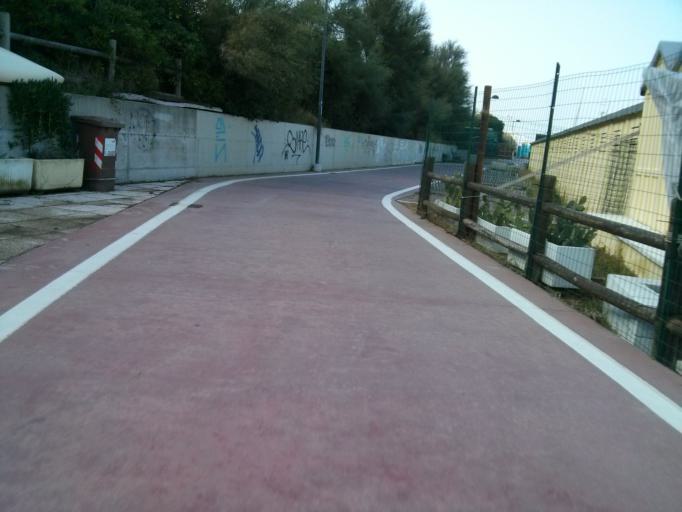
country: IT
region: The Marches
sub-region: Provincia di Pesaro e Urbino
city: Pesaro
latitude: 43.9018
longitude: 12.9350
